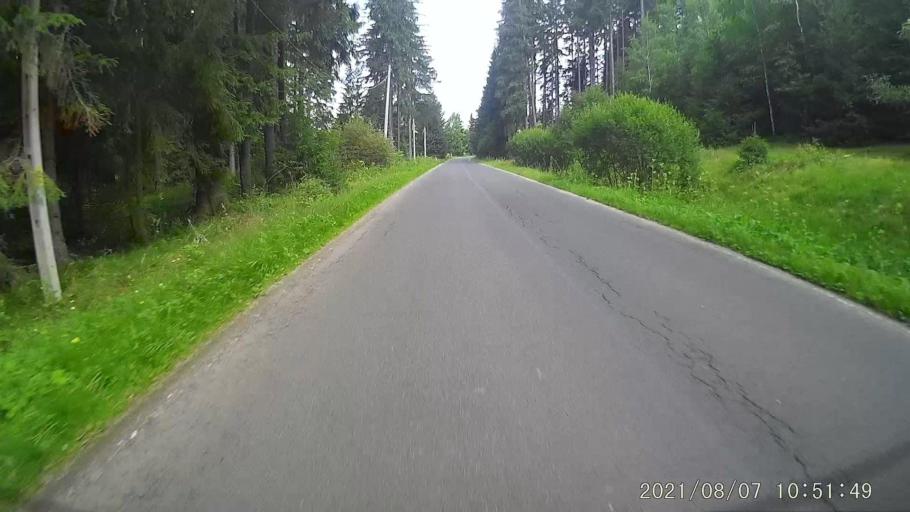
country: CZ
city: Rokytnice v Orlickych Horach
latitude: 50.2861
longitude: 16.4688
